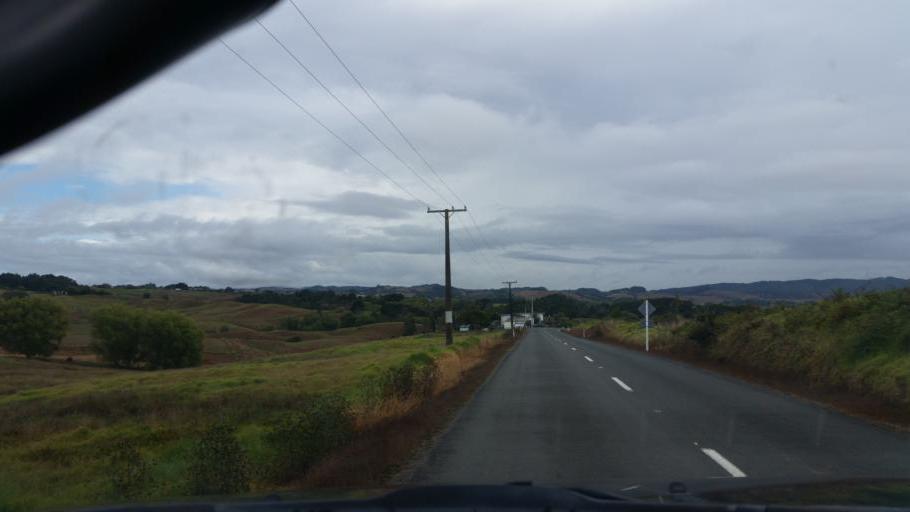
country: NZ
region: Auckland
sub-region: Auckland
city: Wellsford
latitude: -36.1280
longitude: 174.3576
